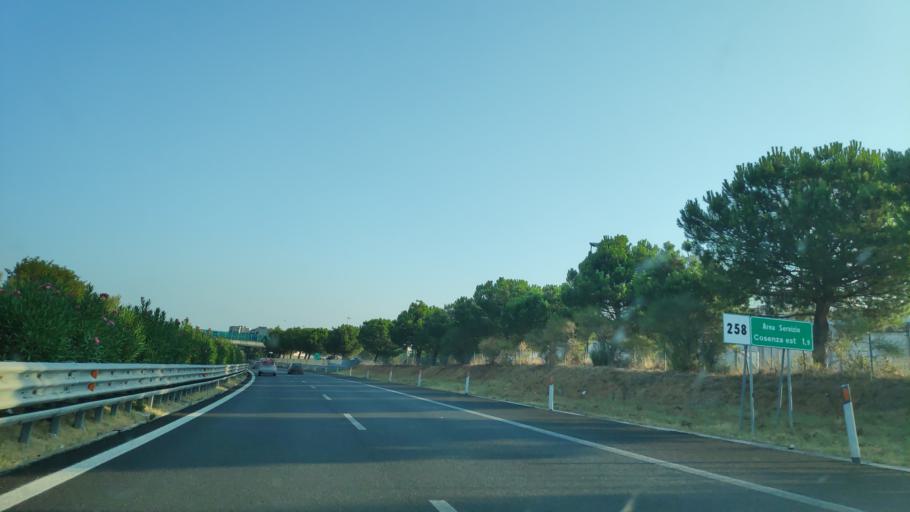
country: IT
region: Calabria
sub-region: Provincia di Cosenza
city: Quattromiglia
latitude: 39.3268
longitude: 16.2398
